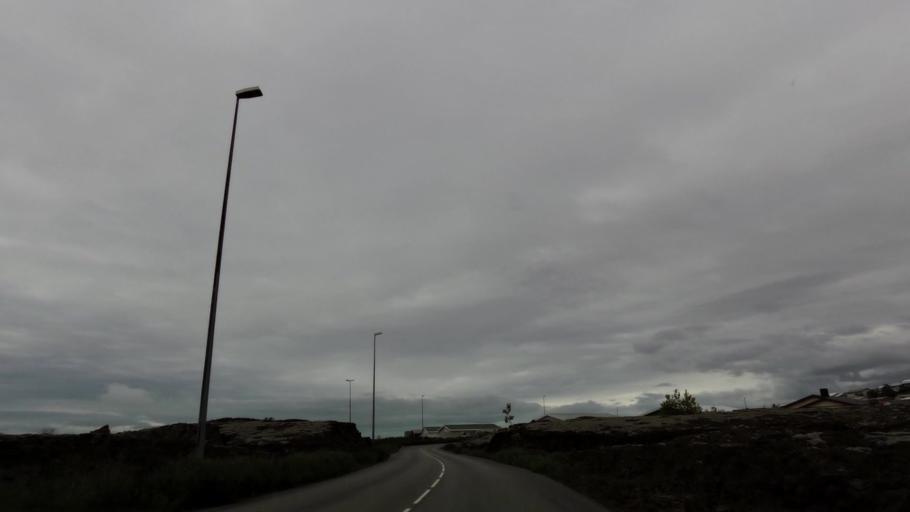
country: IS
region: Capital Region
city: Alftanes
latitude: 64.0536
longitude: -21.9906
